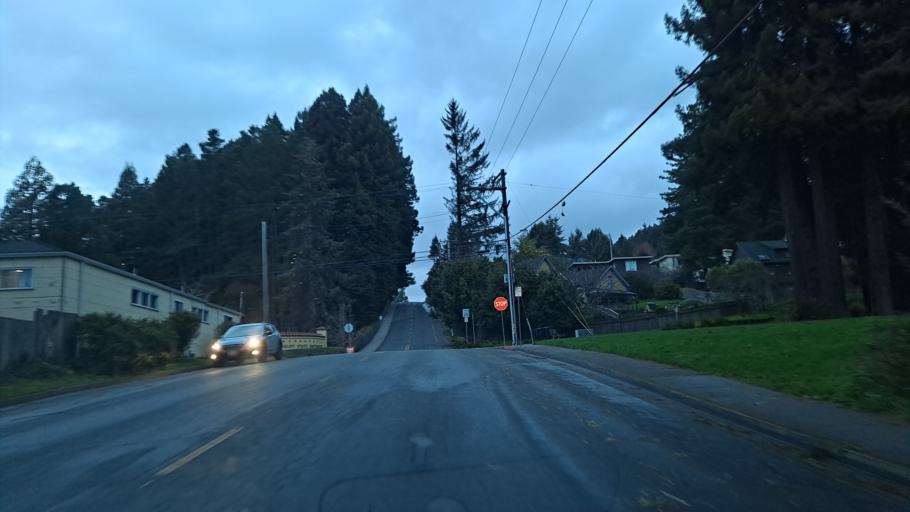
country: US
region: California
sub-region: Humboldt County
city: Arcata
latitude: 40.8708
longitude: -124.0772
